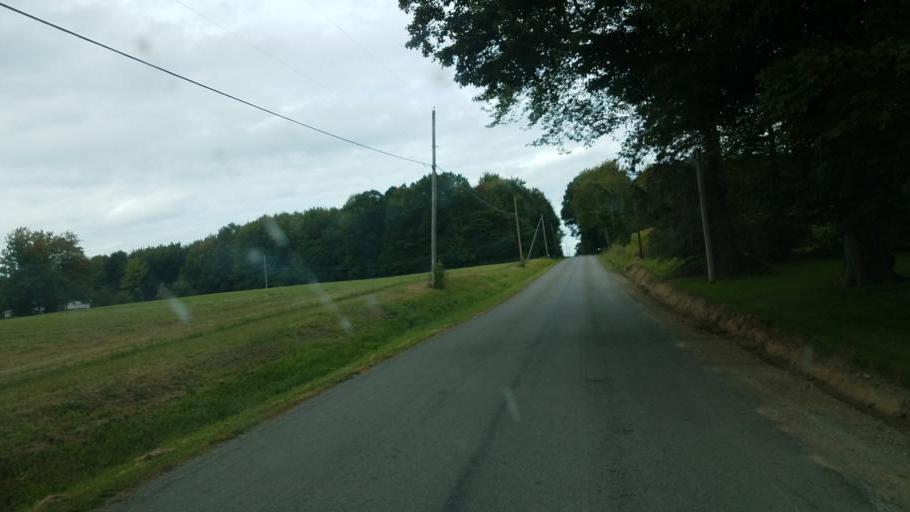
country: US
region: Pennsylvania
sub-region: Mercer County
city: Greenville
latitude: 41.5073
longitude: -80.3860
